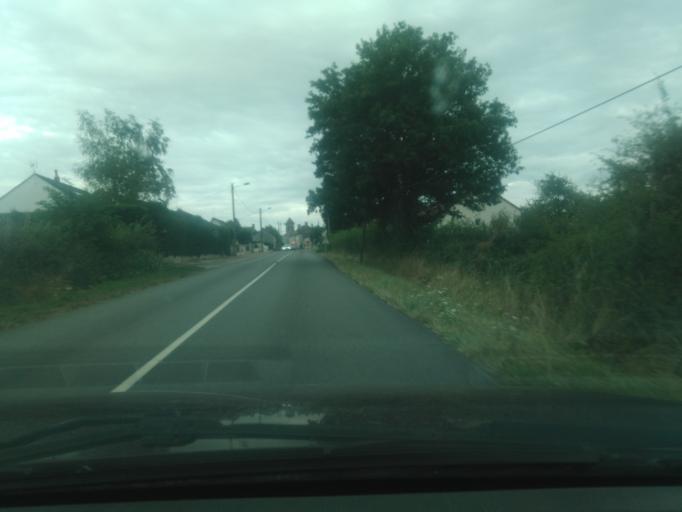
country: FR
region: Bourgogne
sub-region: Departement de la Nievre
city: Dornes
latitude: 46.7763
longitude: 3.3892
